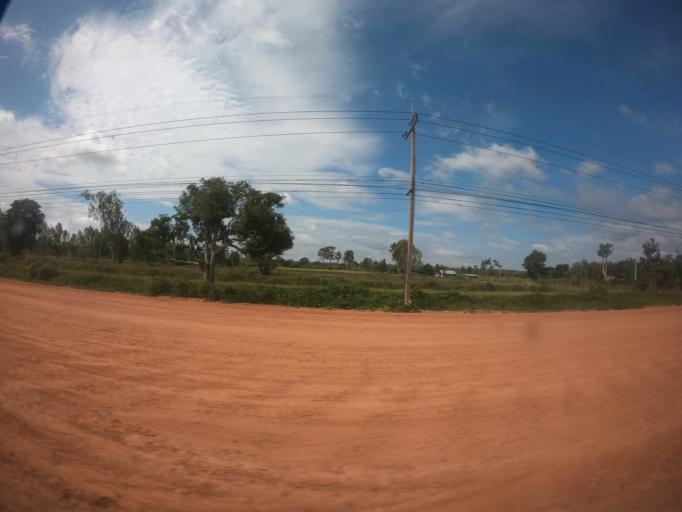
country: TH
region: Surin
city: Kap Choeng
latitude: 14.4568
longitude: 103.6760
